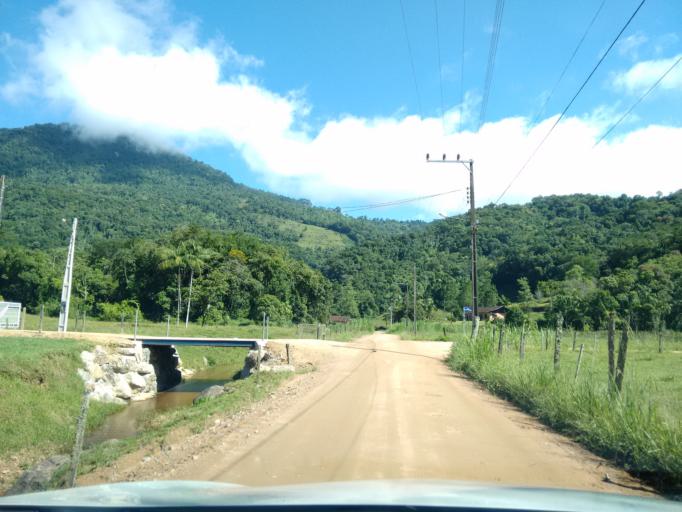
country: BR
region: Santa Catarina
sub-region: Pomerode
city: Pomerode
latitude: -26.7624
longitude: -49.1841
